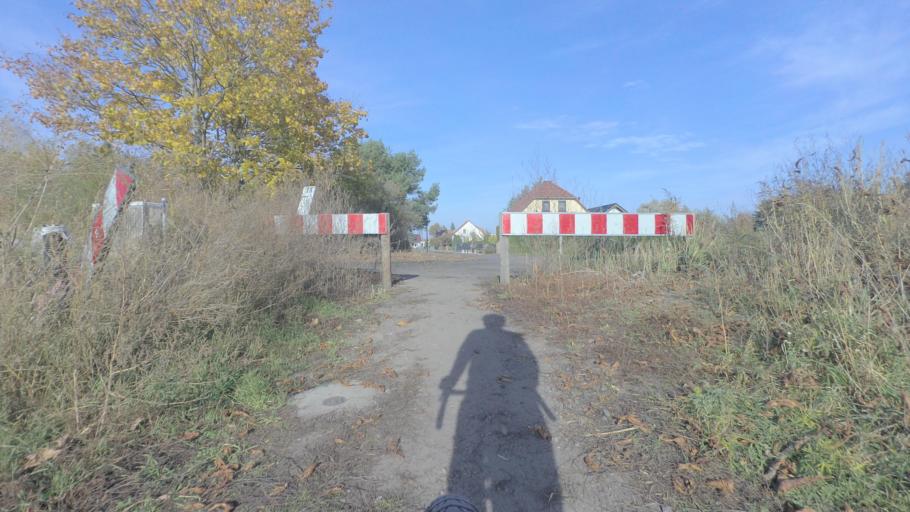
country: DE
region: Brandenburg
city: Zossen
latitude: 52.2209
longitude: 13.4241
